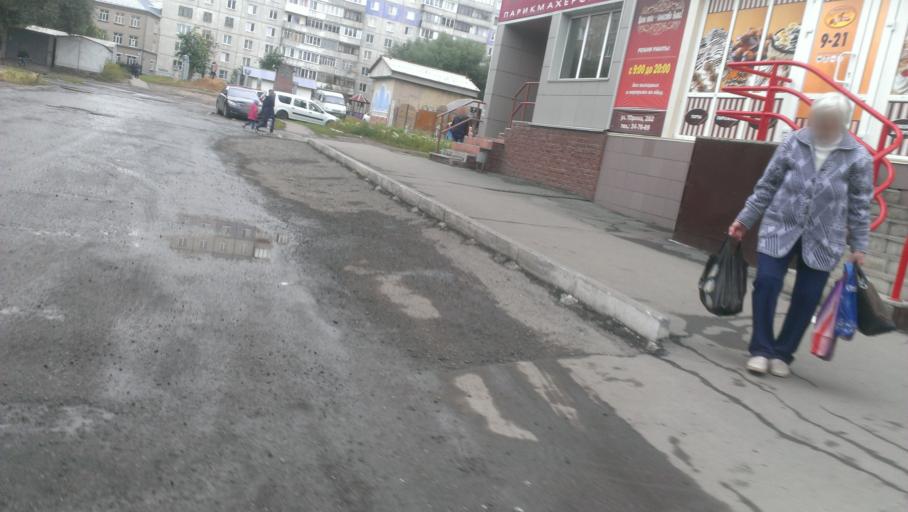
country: RU
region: Altai Krai
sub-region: Gorod Barnaulskiy
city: Barnaul
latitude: 53.3704
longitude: 83.6884
